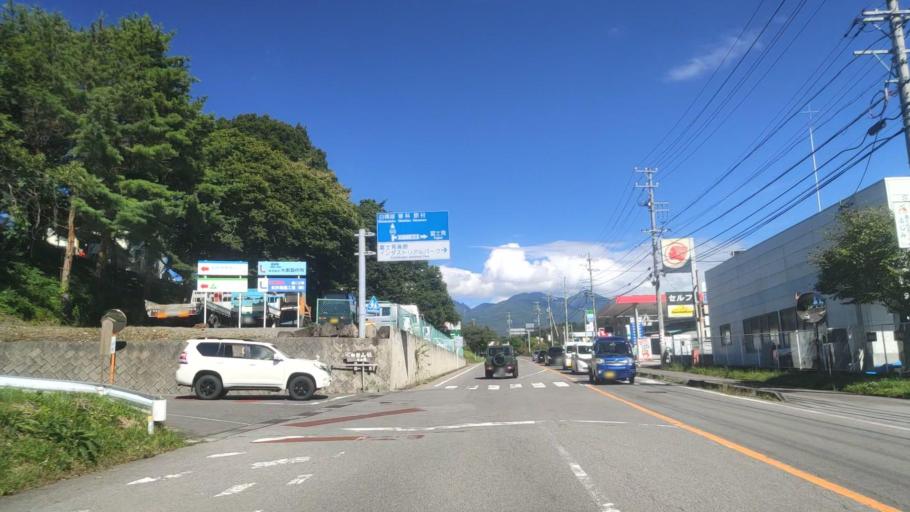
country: JP
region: Nagano
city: Chino
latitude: 35.9371
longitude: 138.2158
